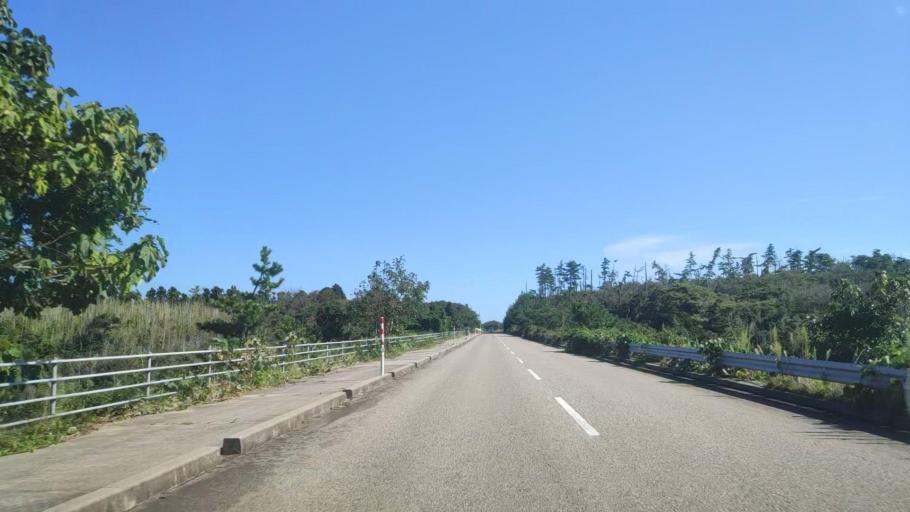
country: JP
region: Ishikawa
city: Hakui
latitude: 37.0742
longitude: 136.7221
